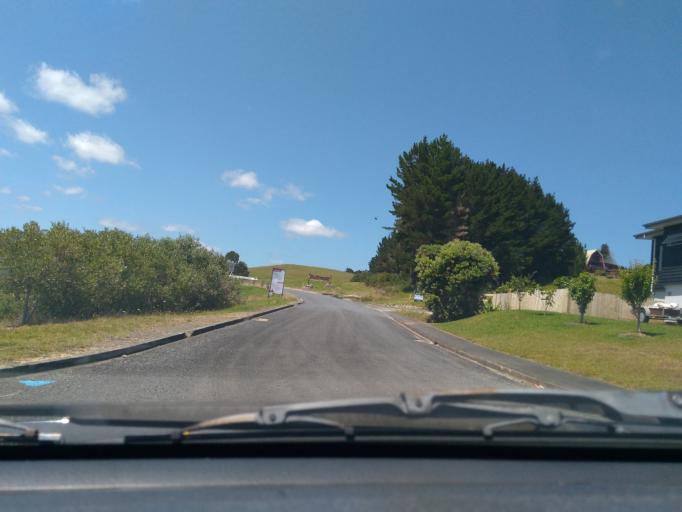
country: NZ
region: Northland
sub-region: Far North District
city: Taipa
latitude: -34.9951
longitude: 173.5113
